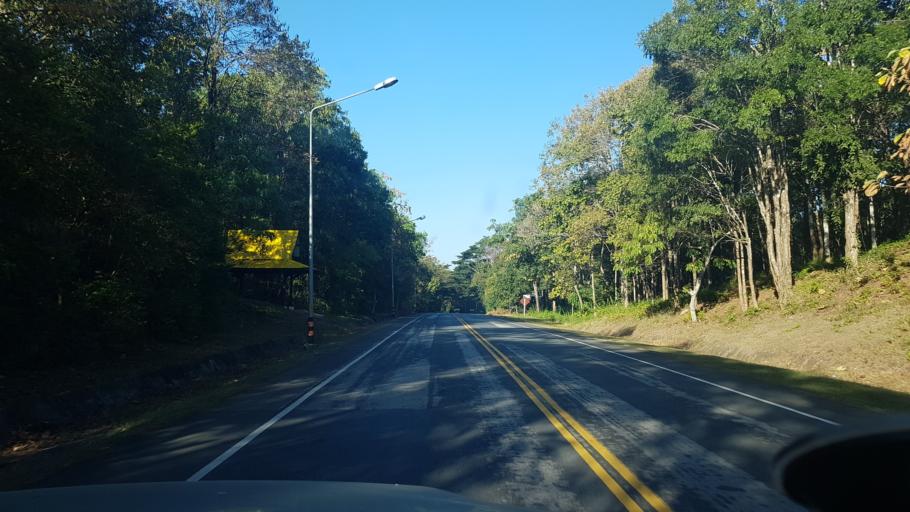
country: TH
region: Phetchabun
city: Lom Sak
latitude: 16.7360
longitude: 101.4323
